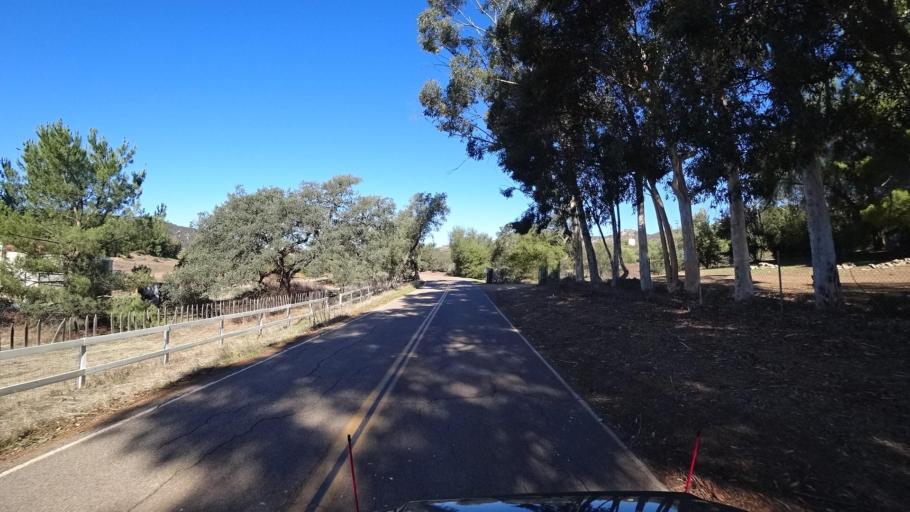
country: US
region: California
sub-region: San Diego County
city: Jamul
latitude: 32.7216
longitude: -116.8054
